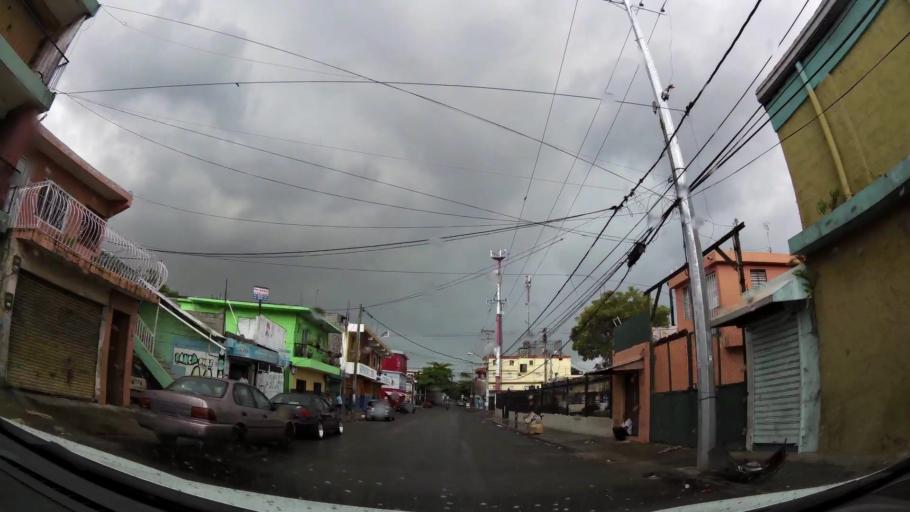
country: DO
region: Nacional
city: Ensanche Luperon
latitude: 18.4959
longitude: -69.9081
